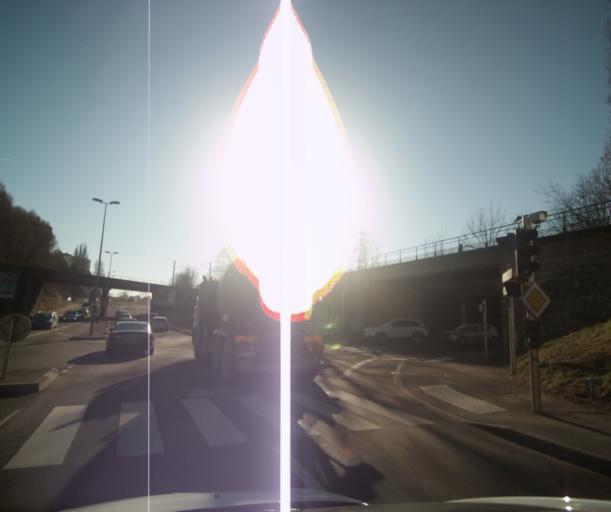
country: FR
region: Franche-Comte
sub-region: Departement du Doubs
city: Pirey
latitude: 47.2347
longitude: 5.9844
